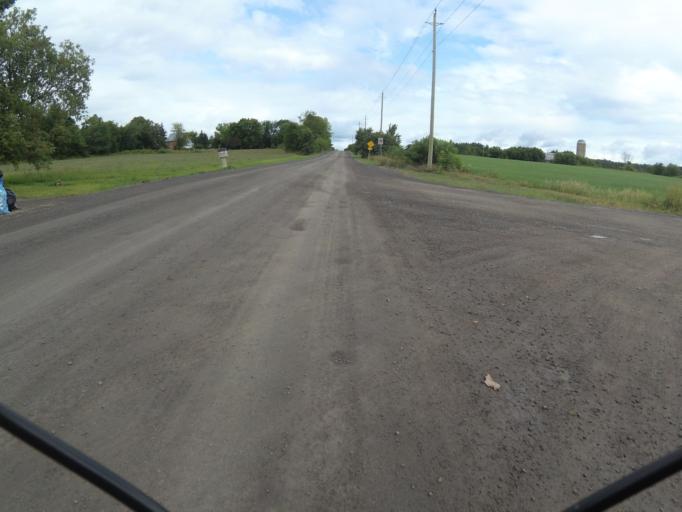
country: CA
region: Ontario
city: Clarence-Rockland
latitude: 45.4752
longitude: -75.3060
